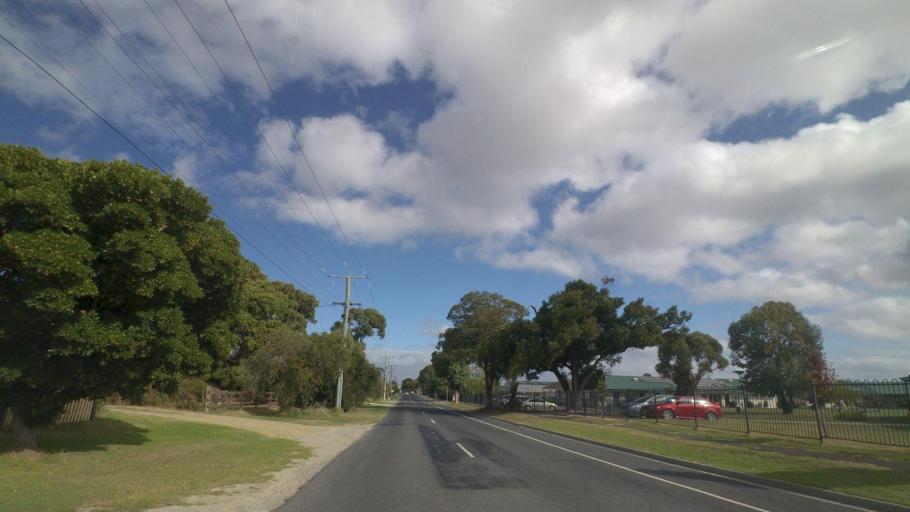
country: AU
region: Victoria
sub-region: Cardinia
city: Garfield
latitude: -38.0822
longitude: 145.6242
